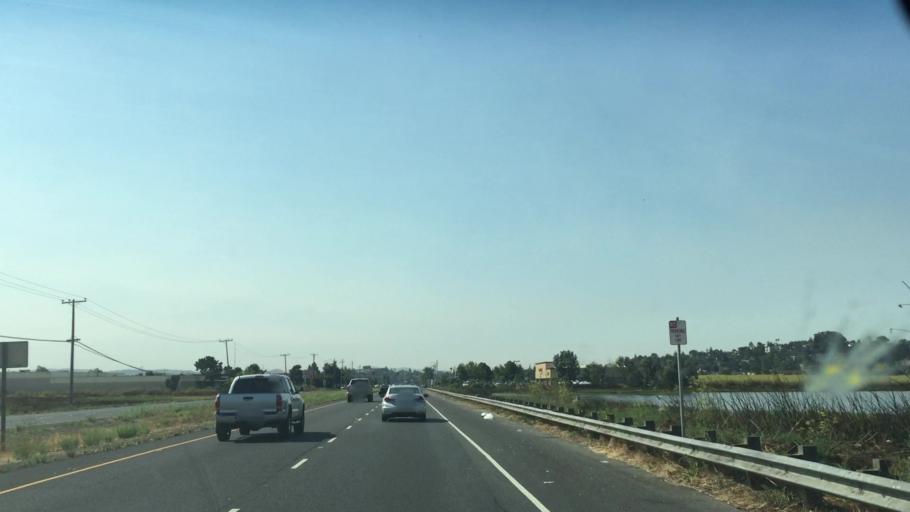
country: US
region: California
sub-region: Solano County
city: Vallejo
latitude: 38.1313
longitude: -122.2561
